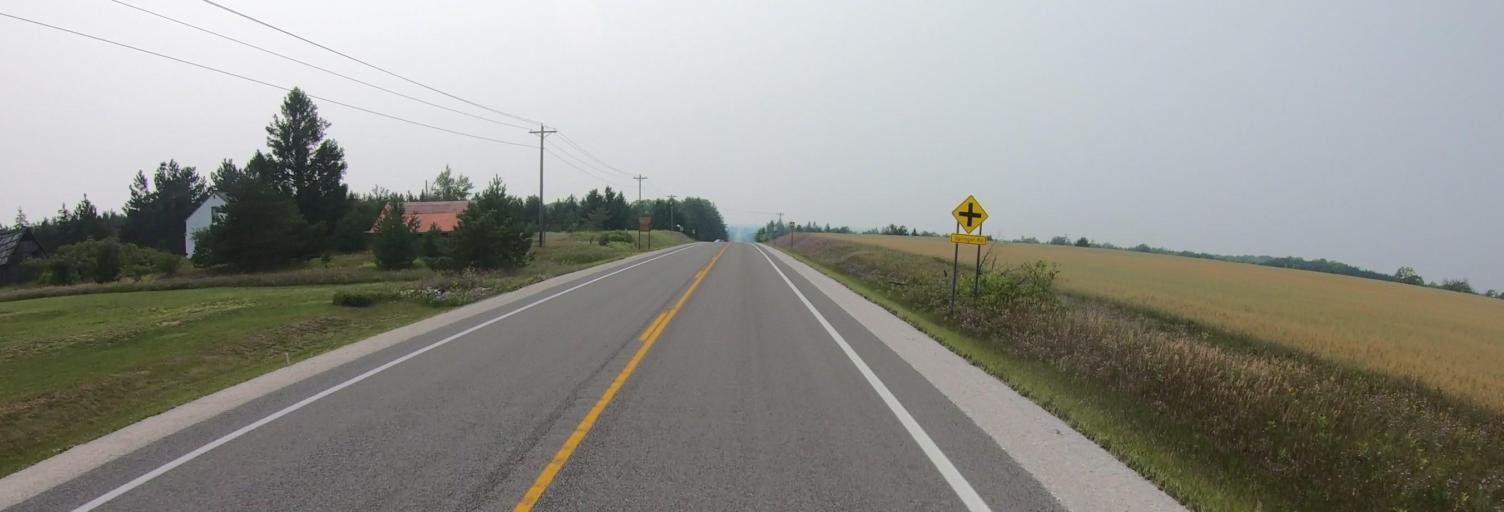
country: US
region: Michigan
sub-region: Chippewa County
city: Sault Ste. Marie
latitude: 46.0722
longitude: -84.1722
